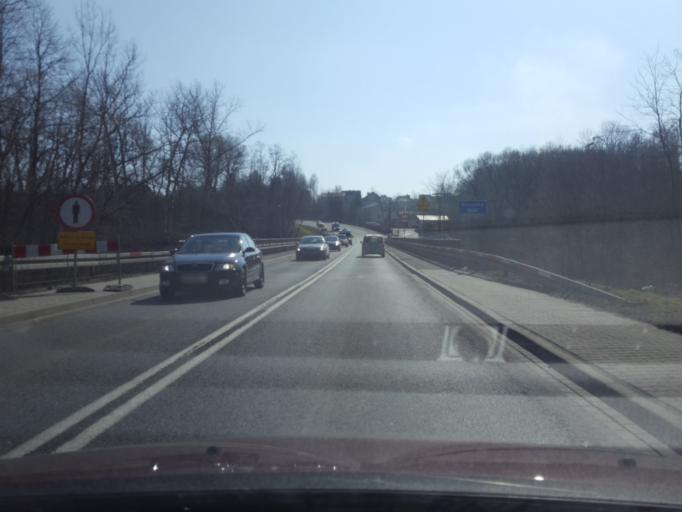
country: PL
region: Lesser Poland Voivodeship
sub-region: Powiat nowosadecki
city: Lososina Dolna
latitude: 49.7397
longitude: 20.6290
